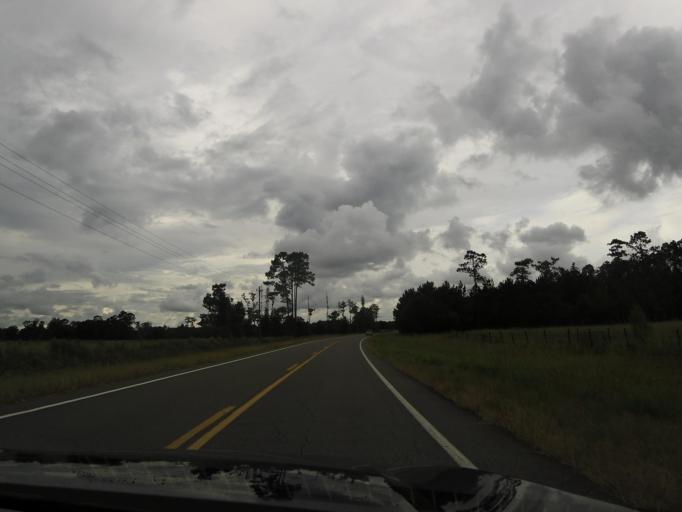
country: US
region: Florida
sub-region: Baker County
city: Macclenny
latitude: 30.3973
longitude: -82.1831
